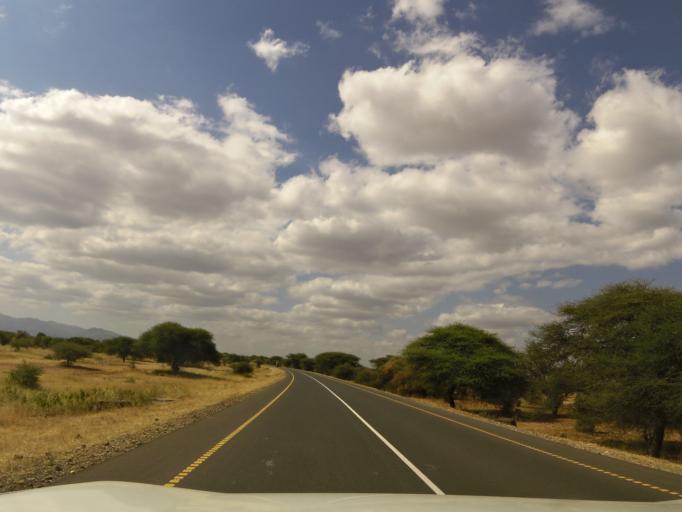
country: TZ
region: Arusha
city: Mto wa Mbu
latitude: -3.5785
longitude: 36.0726
